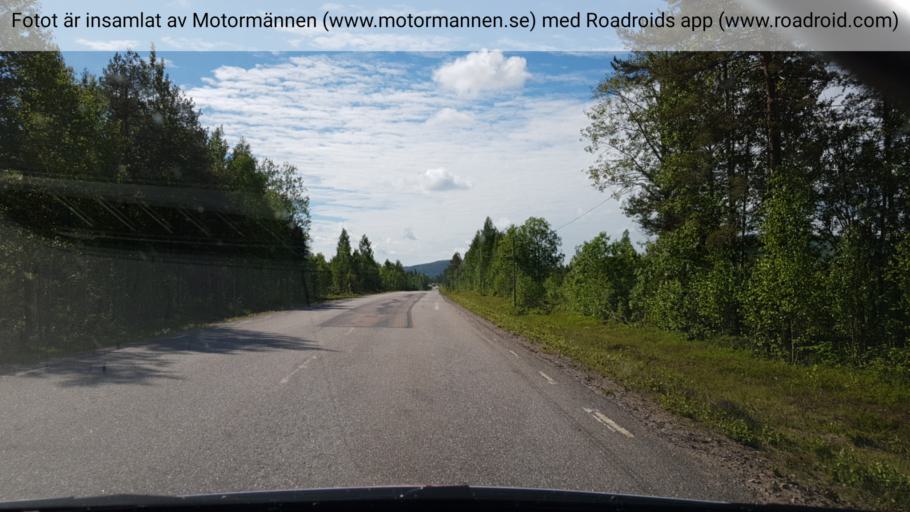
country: FI
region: Lapland
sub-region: Torniolaakso
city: Pello
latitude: 66.6835
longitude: 23.8398
